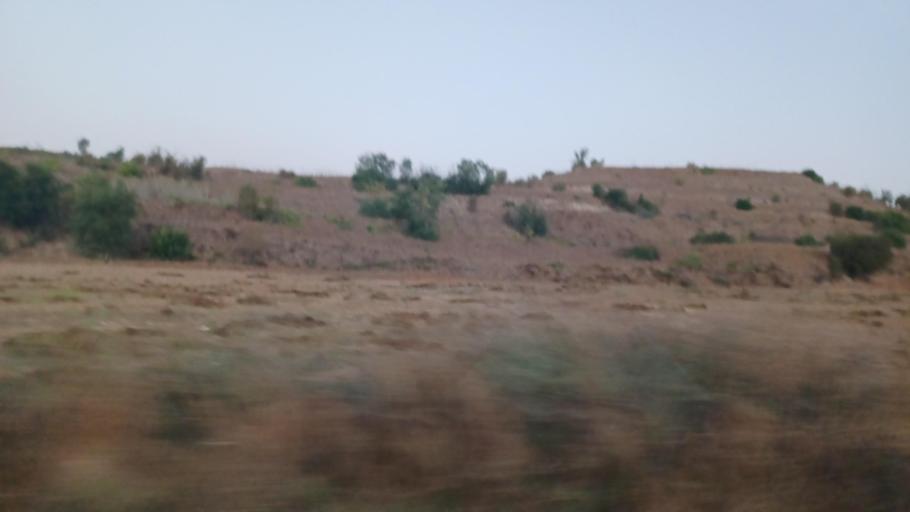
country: CY
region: Pafos
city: Mesogi
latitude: 34.8530
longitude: 32.5424
